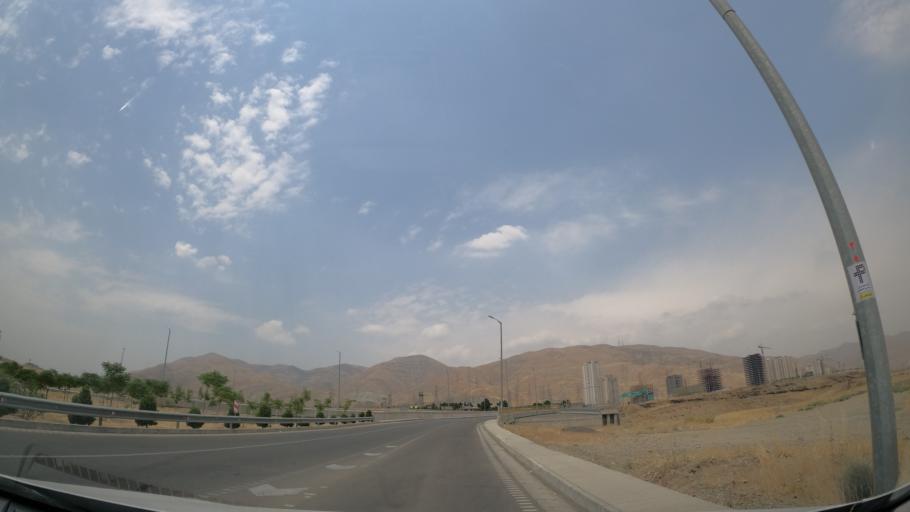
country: IR
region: Tehran
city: Shahr-e Qods
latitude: 35.7450
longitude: 51.1280
